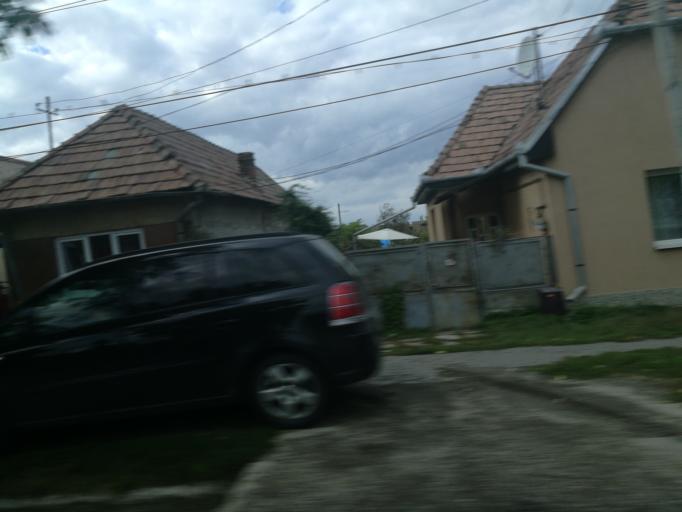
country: RO
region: Mures
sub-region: Comuna Cristesti
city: Cristesti
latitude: 46.5058
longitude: 24.4987
